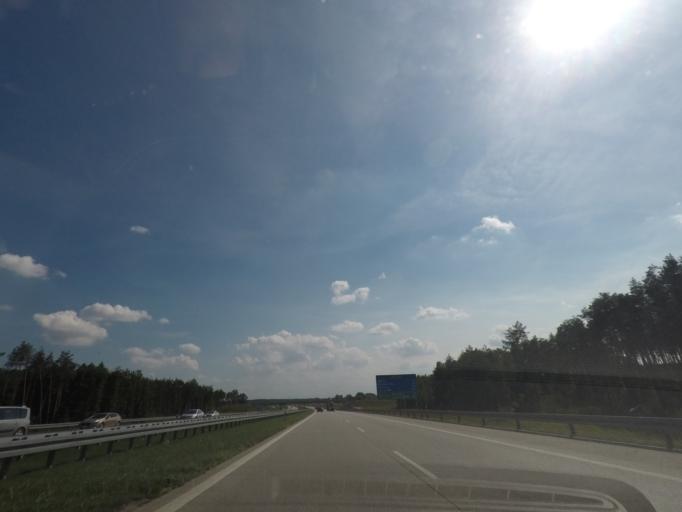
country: PL
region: Lodz Voivodeship
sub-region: Powiat lodzki wschodni
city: Tuszyn
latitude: 51.6280
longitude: 19.5682
